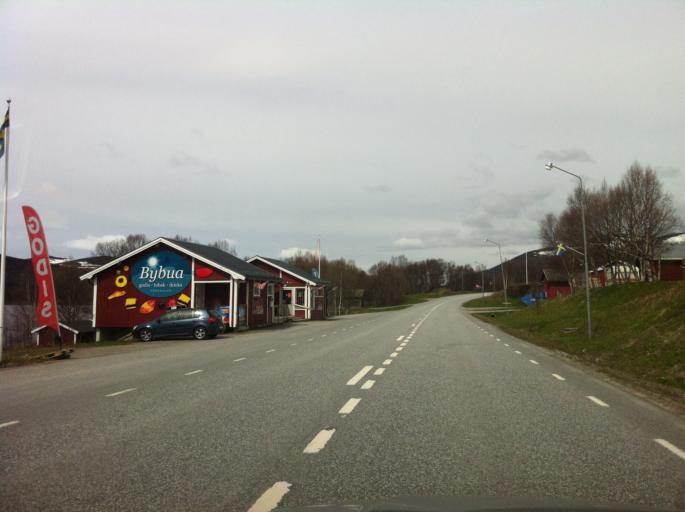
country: NO
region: Sor-Trondelag
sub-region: Tydal
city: Aas
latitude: 62.5401
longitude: 12.3423
